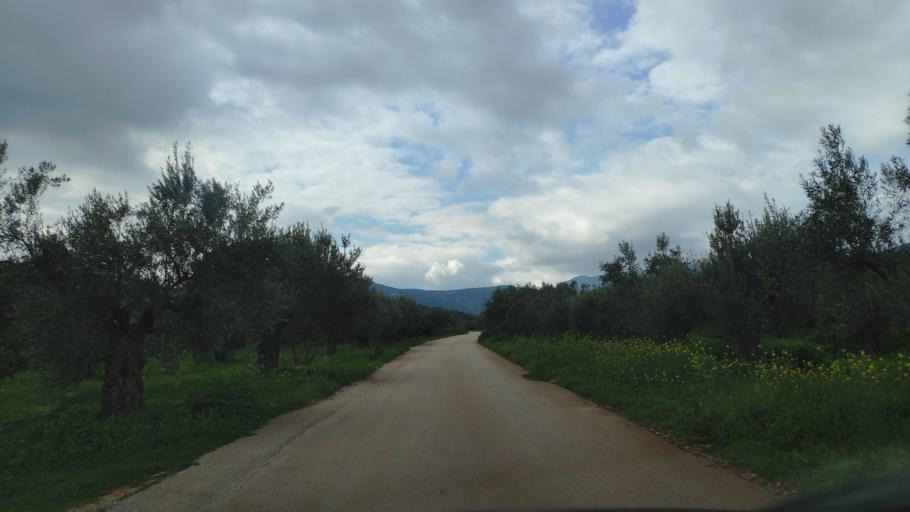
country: GR
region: Peloponnese
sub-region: Nomos Argolidos
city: Nea Kios
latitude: 37.5380
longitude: 22.7016
